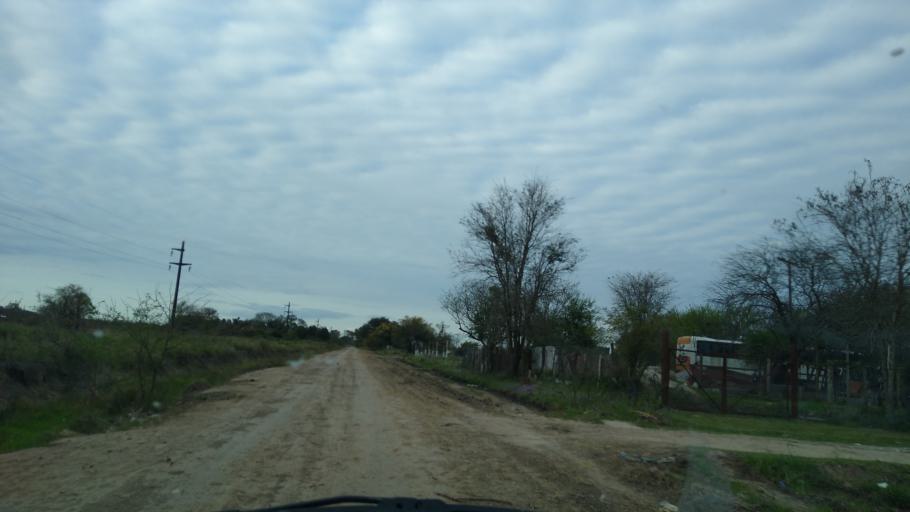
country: AR
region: Chaco
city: Fontana
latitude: -27.3852
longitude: -59.0438
